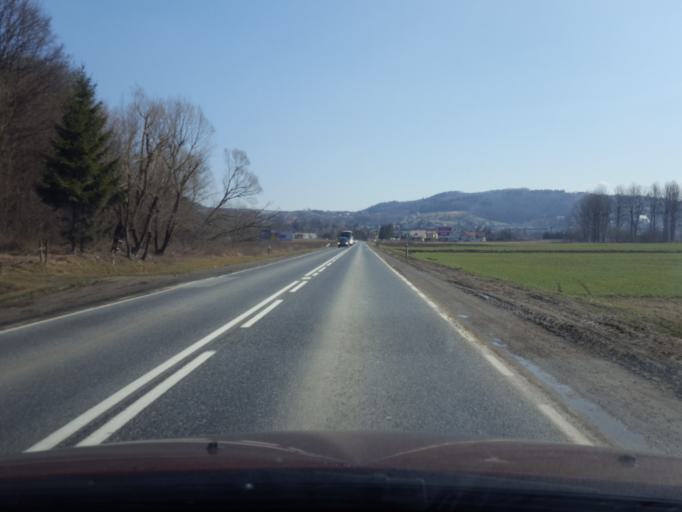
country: PL
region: Lesser Poland Voivodeship
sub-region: Powiat nowosadecki
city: Chelmiec
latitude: 49.6753
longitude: 20.6674
